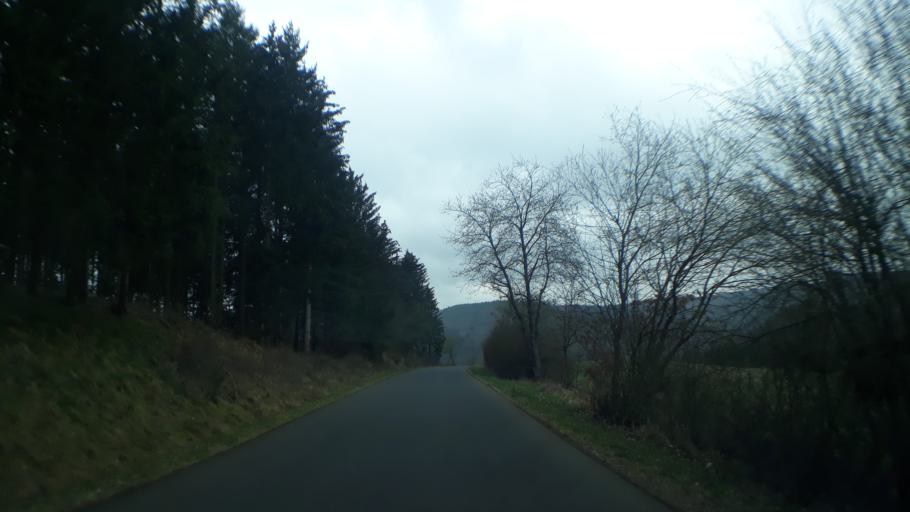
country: DE
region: North Rhine-Westphalia
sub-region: Regierungsbezirk Koln
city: Schleiden
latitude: 50.5418
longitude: 6.4970
